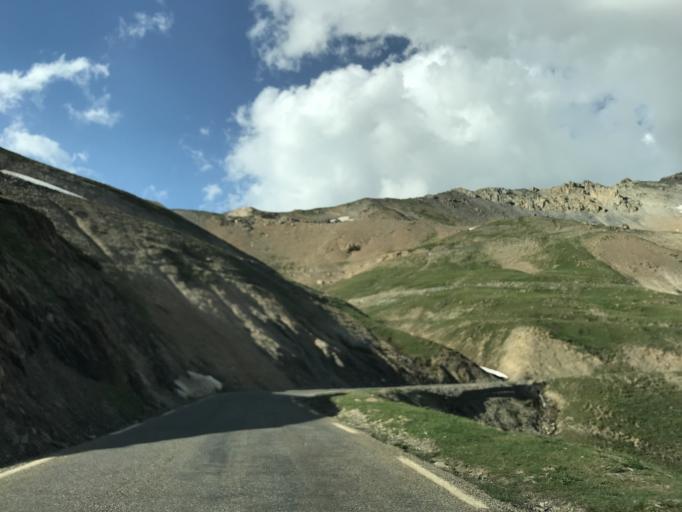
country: FR
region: Rhone-Alpes
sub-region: Departement de la Savoie
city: Valloire
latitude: 45.0602
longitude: 6.4069
